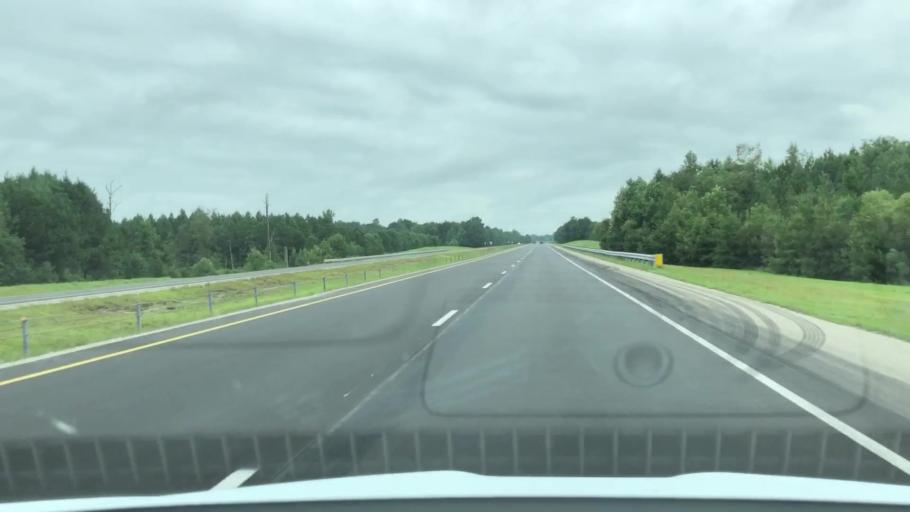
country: US
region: North Carolina
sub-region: Wilson County
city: Lucama
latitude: 35.6056
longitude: -77.9803
